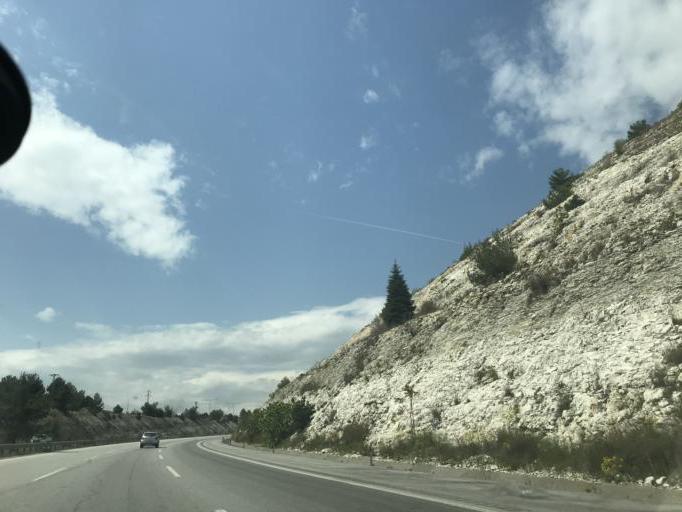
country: TR
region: Mersin
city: Tarsus
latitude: 37.1376
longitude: 34.8453
